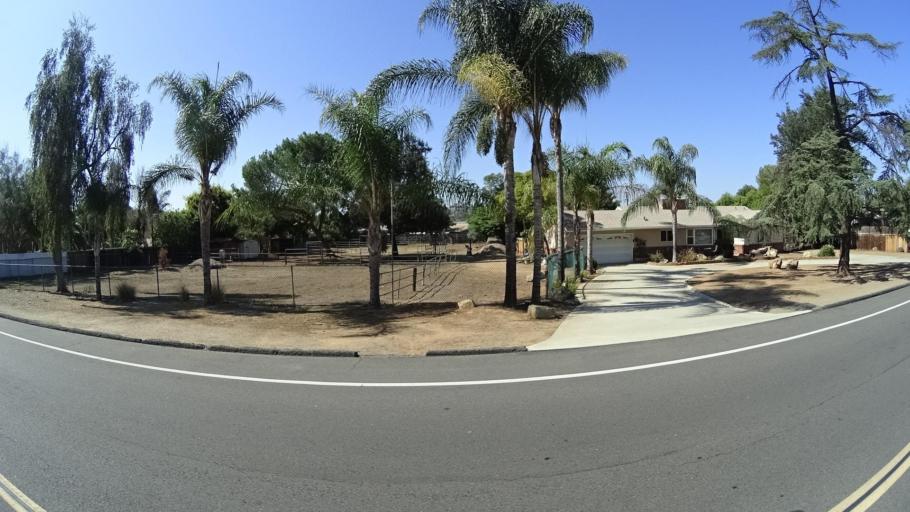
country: US
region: California
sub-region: San Diego County
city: Granite Hills
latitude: 32.7905
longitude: -116.9190
